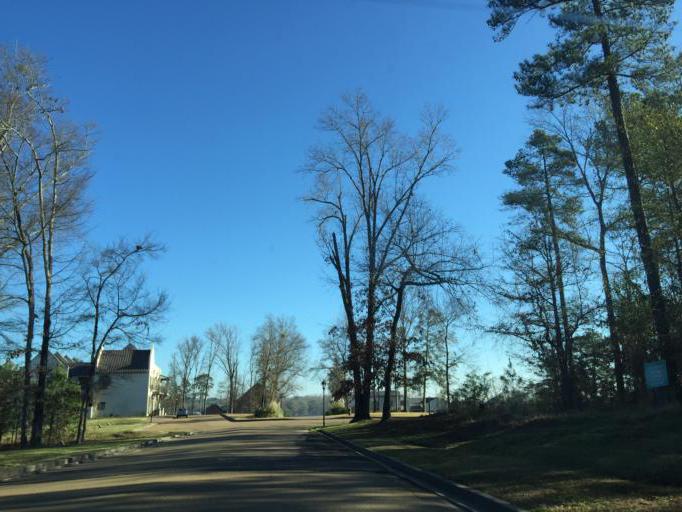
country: US
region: Mississippi
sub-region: Madison County
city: Madison
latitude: 32.4590
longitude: -90.0550
